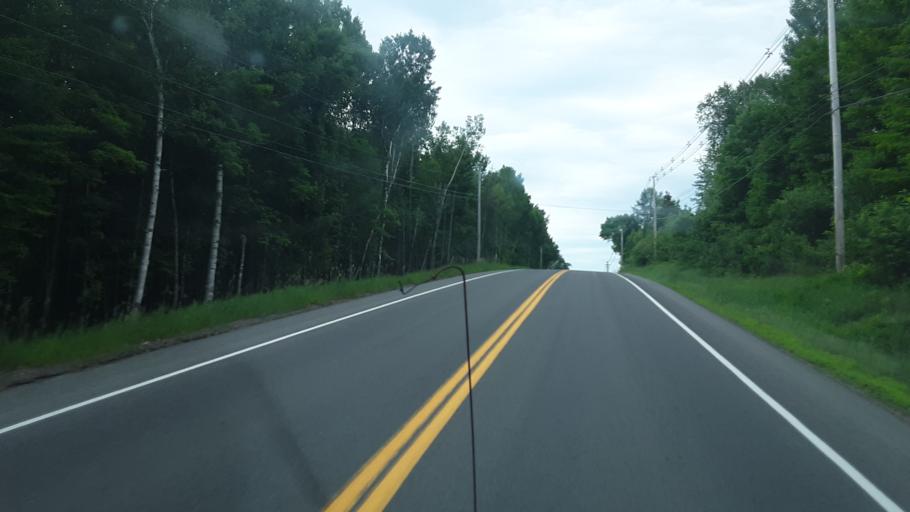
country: US
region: Maine
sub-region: Penobscot County
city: Patten
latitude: 45.8830
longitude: -68.4178
